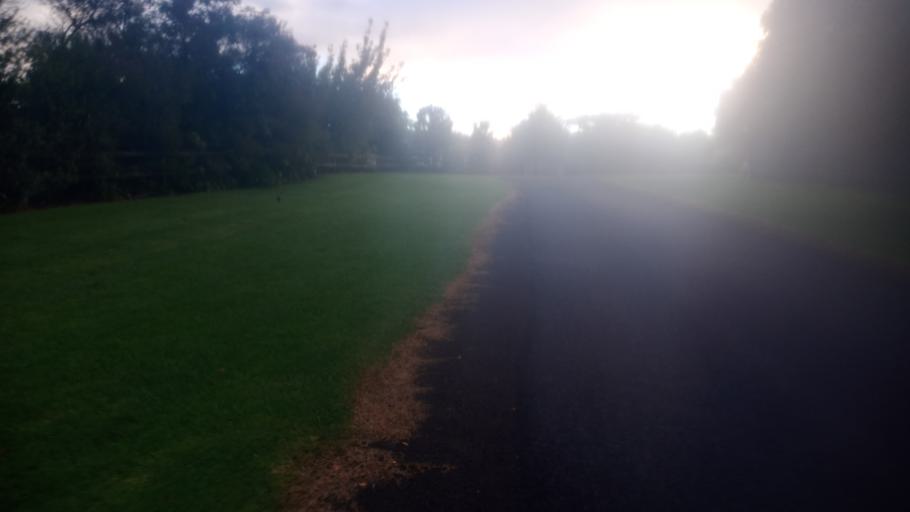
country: NZ
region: Gisborne
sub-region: Gisborne District
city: Gisborne
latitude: -38.6411
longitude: 177.9886
